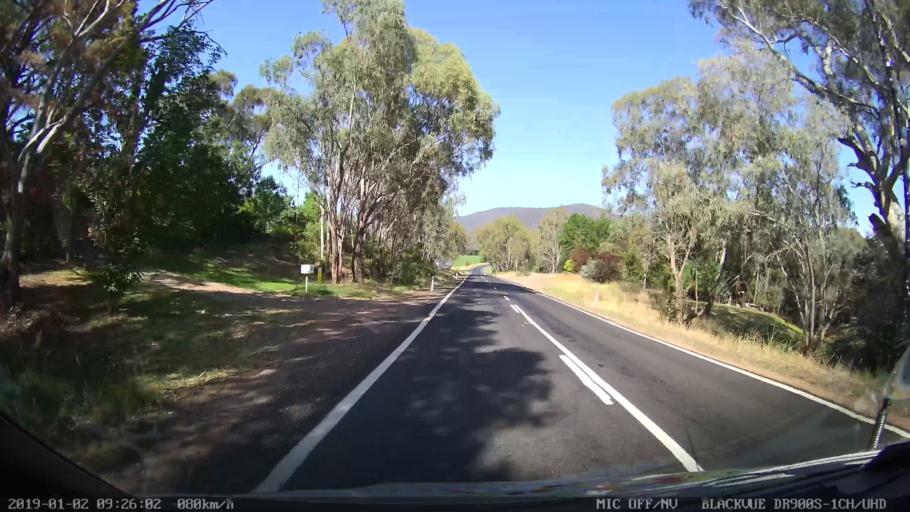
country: AU
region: New South Wales
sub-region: Tumut Shire
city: Tumut
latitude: -35.3648
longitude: 148.2781
